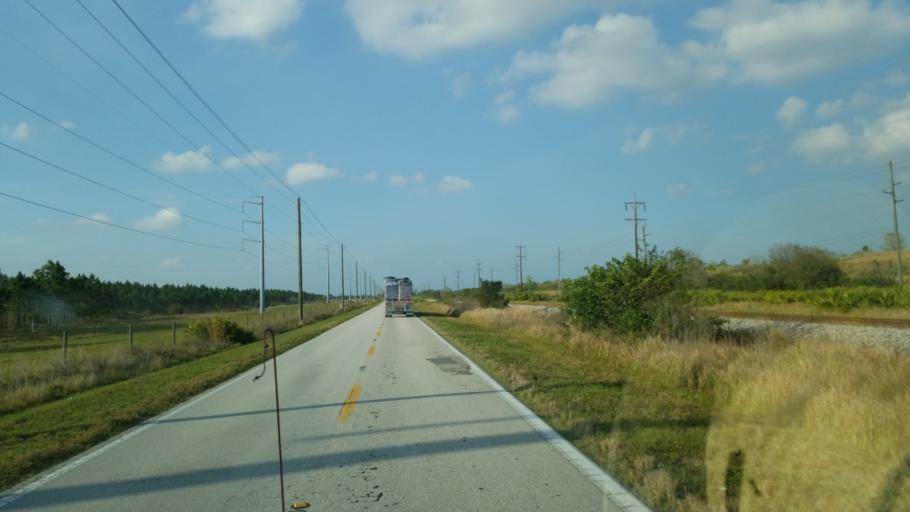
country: US
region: Florida
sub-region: Hardee County
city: Bowling Green
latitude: 27.7043
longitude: -81.9592
